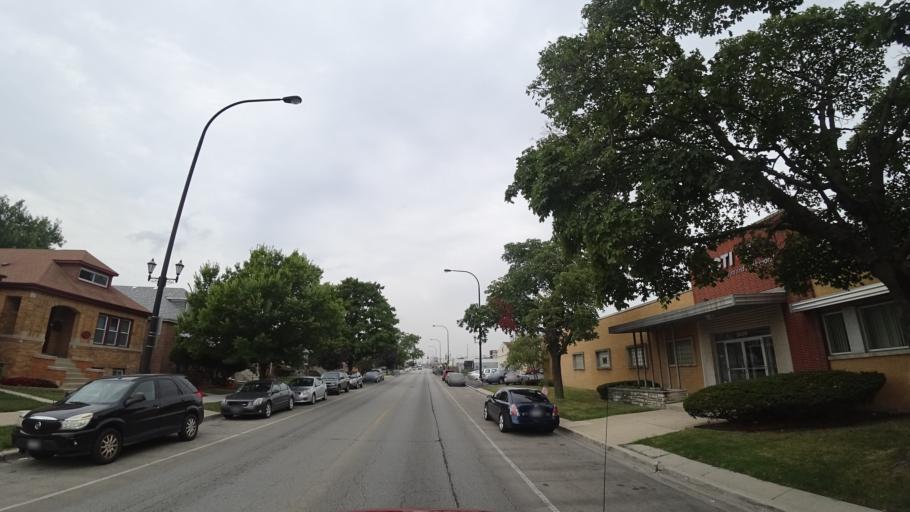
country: US
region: Illinois
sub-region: Cook County
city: Cicero
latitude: 41.8364
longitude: -87.7613
